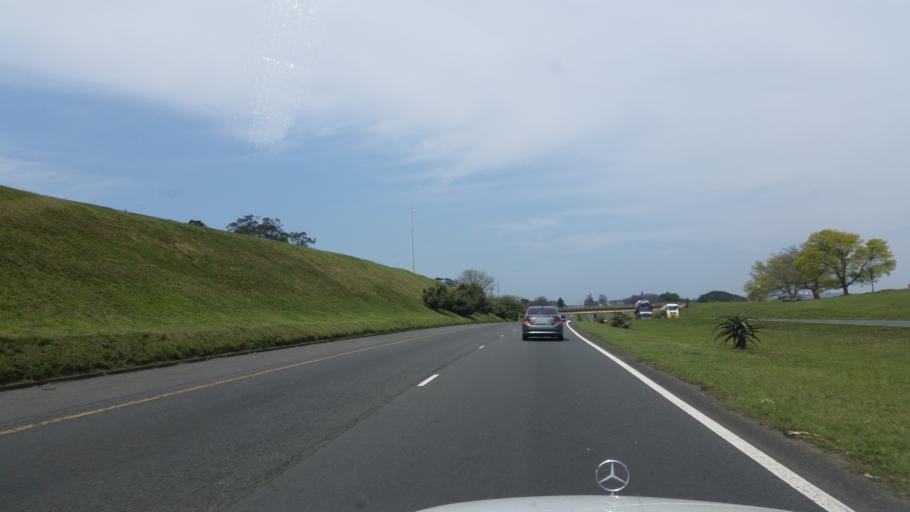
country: ZA
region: KwaZulu-Natal
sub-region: uMgungundlovu District Municipality
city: Camperdown
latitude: -29.7303
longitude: 30.5350
